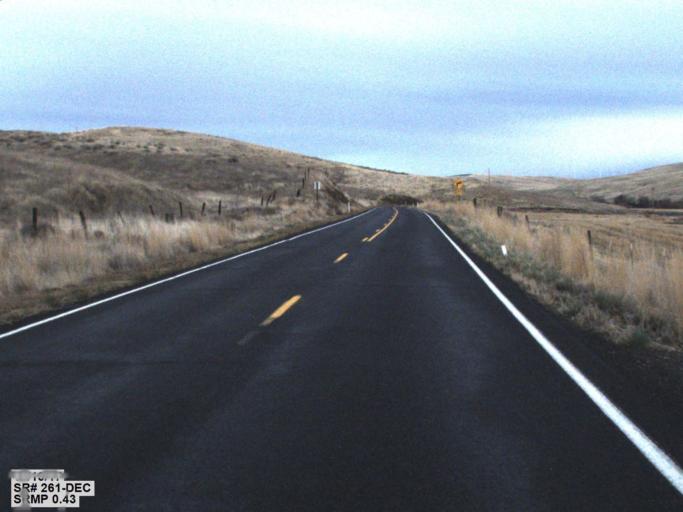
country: US
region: Washington
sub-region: Columbia County
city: Dayton
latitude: 46.5126
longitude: -117.9773
